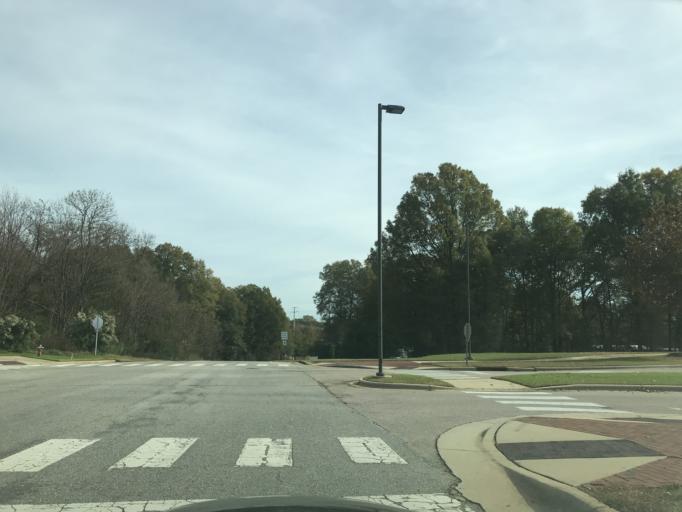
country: US
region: North Carolina
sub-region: Wake County
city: West Raleigh
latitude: 35.7747
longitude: -78.6720
